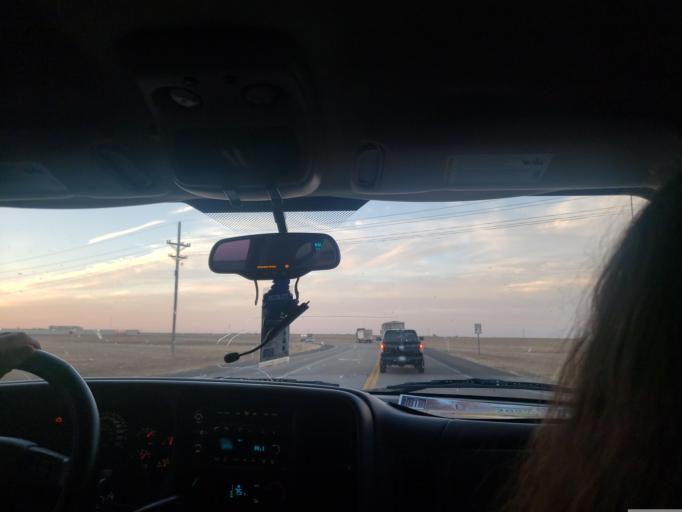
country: US
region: Kansas
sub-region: Seward County
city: Liberal
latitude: 37.0686
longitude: -100.9060
